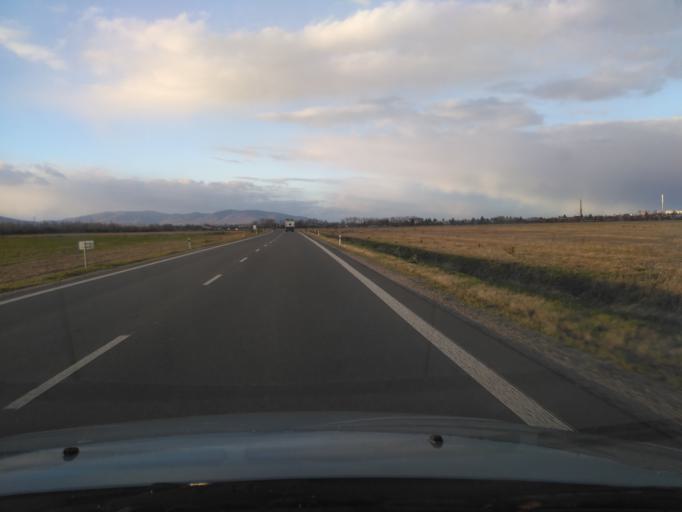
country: SK
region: Kosicky
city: Trebisov
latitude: 48.6128
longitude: 21.7073
